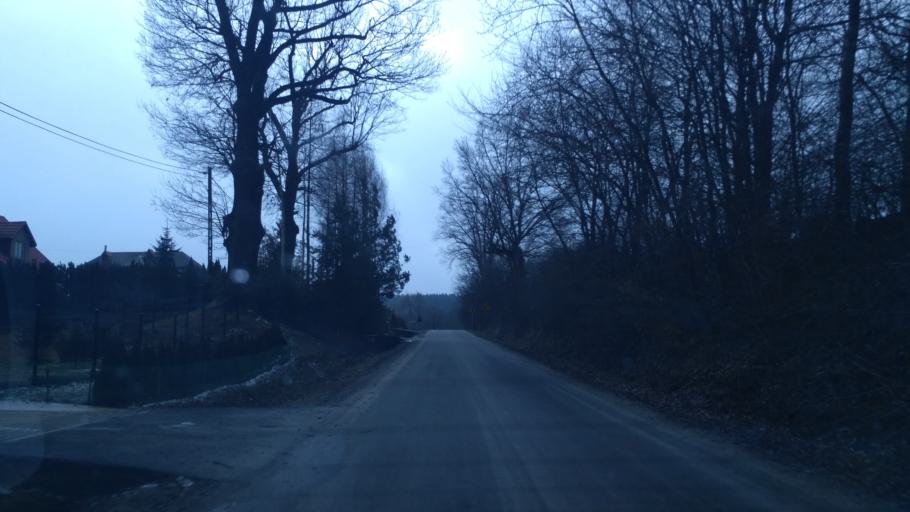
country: PL
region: Subcarpathian Voivodeship
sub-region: Powiat rzeszowski
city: Hyzne
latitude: 49.9036
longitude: 22.1962
